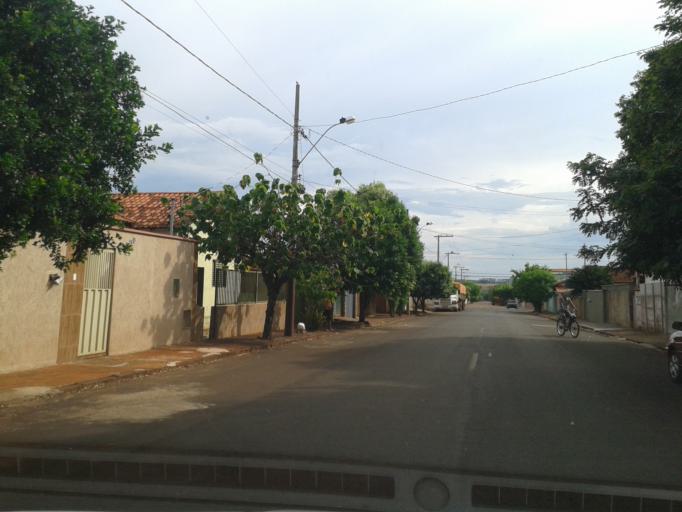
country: BR
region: Minas Gerais
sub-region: Centralina
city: Centralina
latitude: -18.7210
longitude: -49.2041
